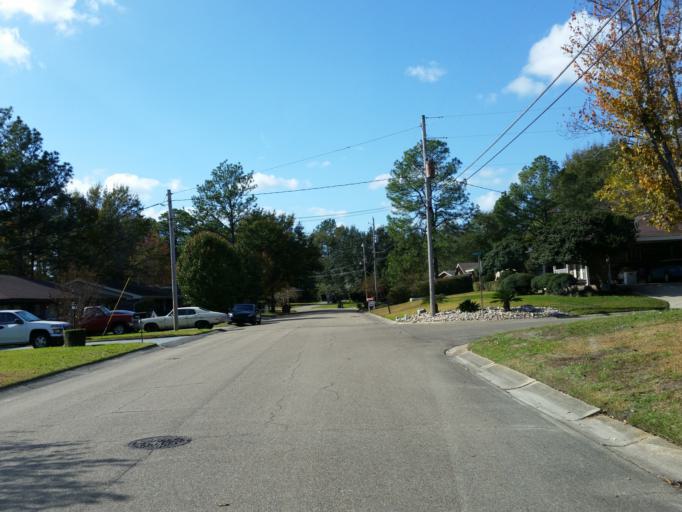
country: US
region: Mississippi
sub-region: Lamar County
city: West Hattiesburg
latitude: 31.3098
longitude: -89.3376
